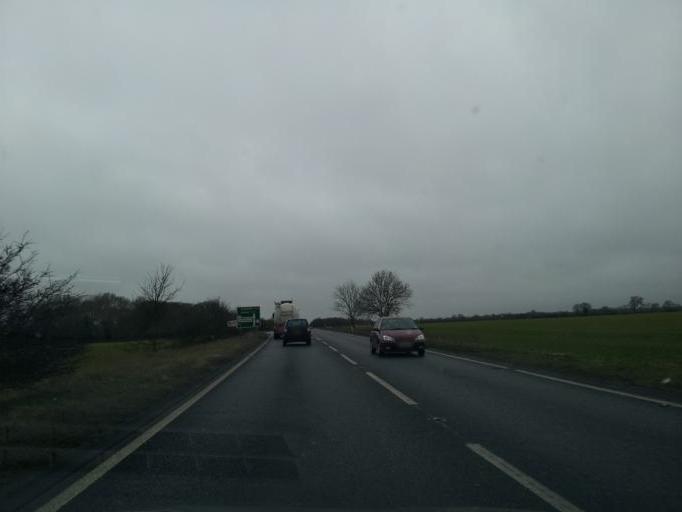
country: GB
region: England
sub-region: Essex
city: Great Bentley
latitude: 51.8918
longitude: 1.0644
